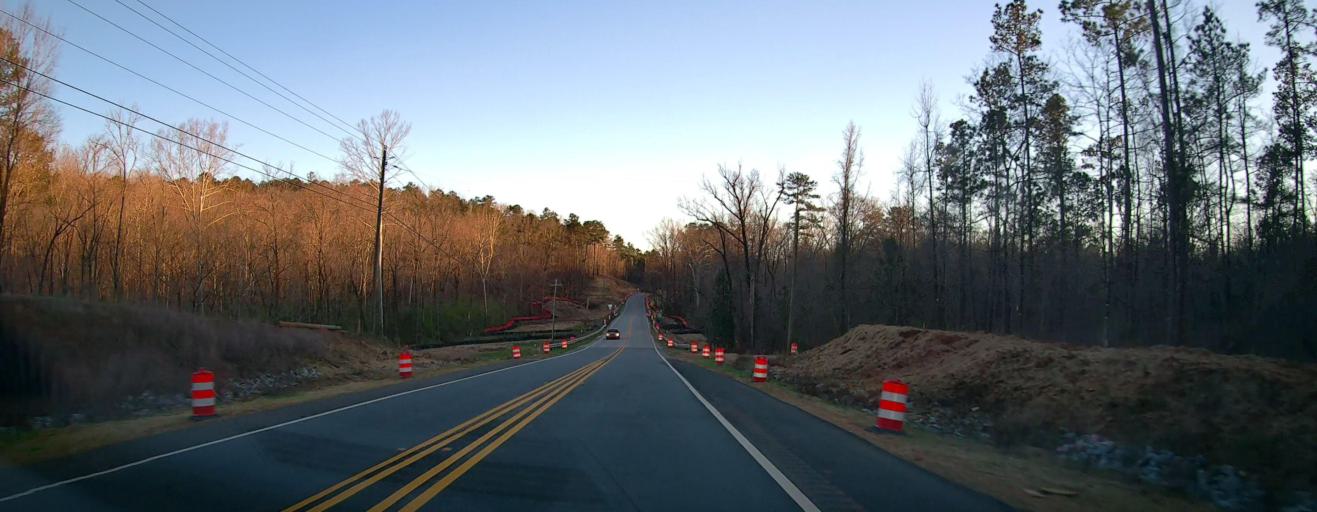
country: US
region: Alabama
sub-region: Lee County
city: Smiths Station
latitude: 32.6023
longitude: -85.0256
